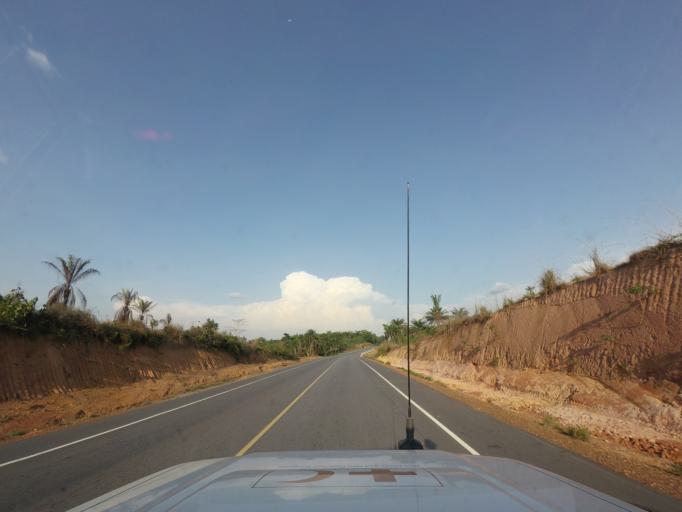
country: LR
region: Bong
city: Gbarnga
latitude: 7.0036
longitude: -9.4107
